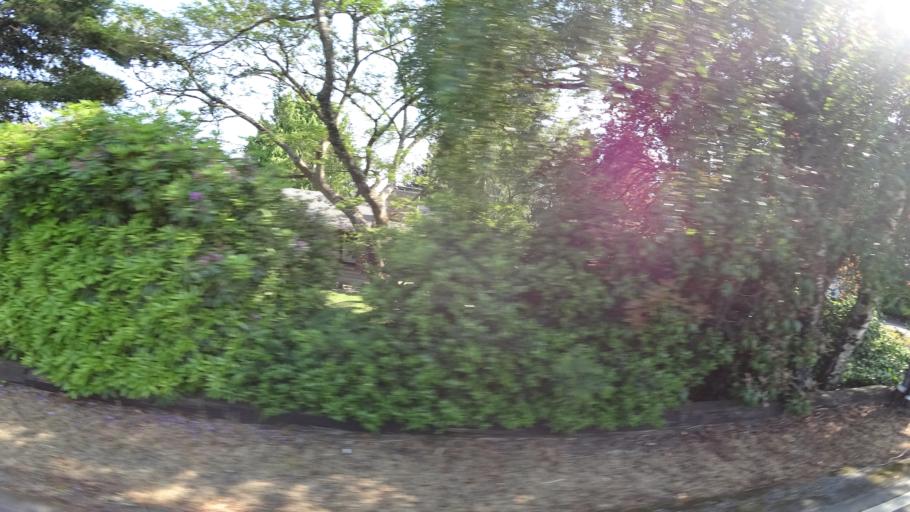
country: US
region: Oregon
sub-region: Clackamas County
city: Happy Valley
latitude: 45.4541
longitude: -122.5304
